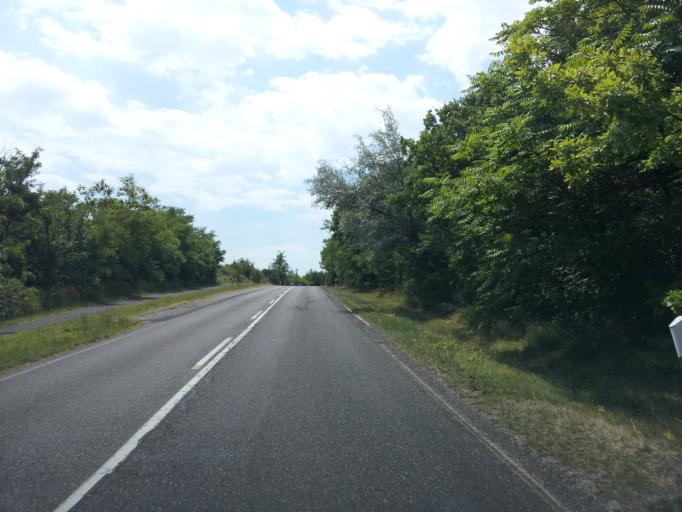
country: HU
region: Somogy
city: Balatonszarszo
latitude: 46.8929
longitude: 17.7731
